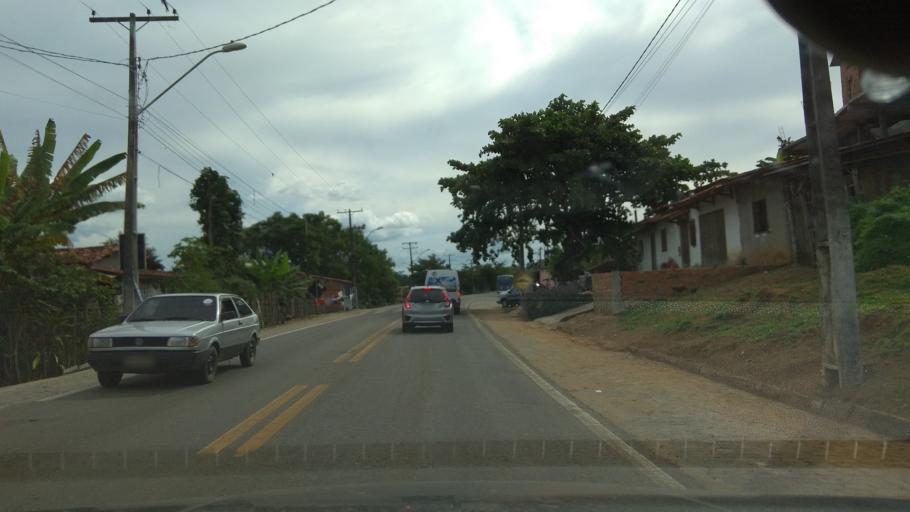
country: BR
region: Bahia
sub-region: Ubata
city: Ubata
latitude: -14.2081
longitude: -39.6001
